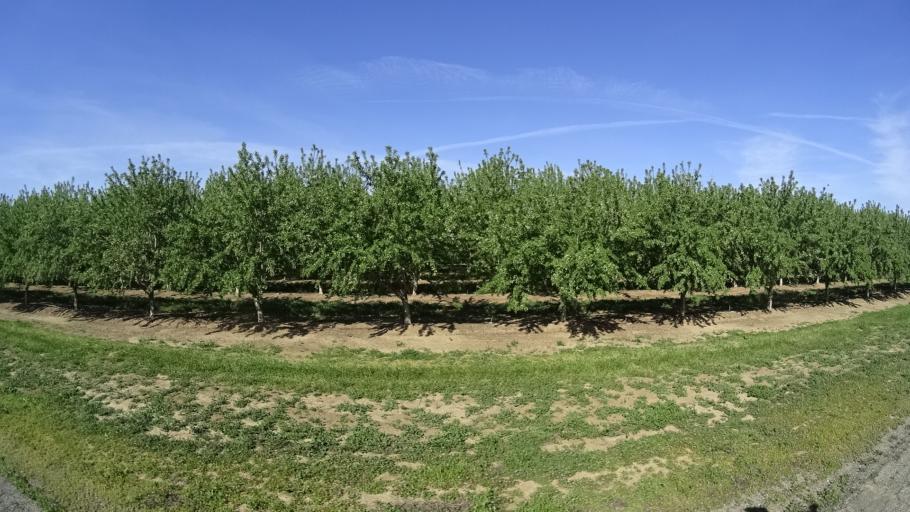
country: US
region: California
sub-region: Glenn County
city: Willows
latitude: 39.6266
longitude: -122.2161
